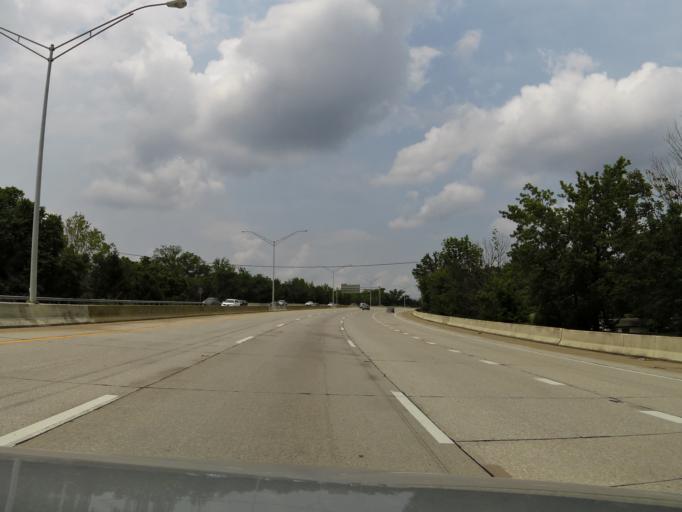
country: US
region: Kentucky
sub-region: Jefferson County
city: Beechwood Village
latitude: 38.2571
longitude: -85.6219
